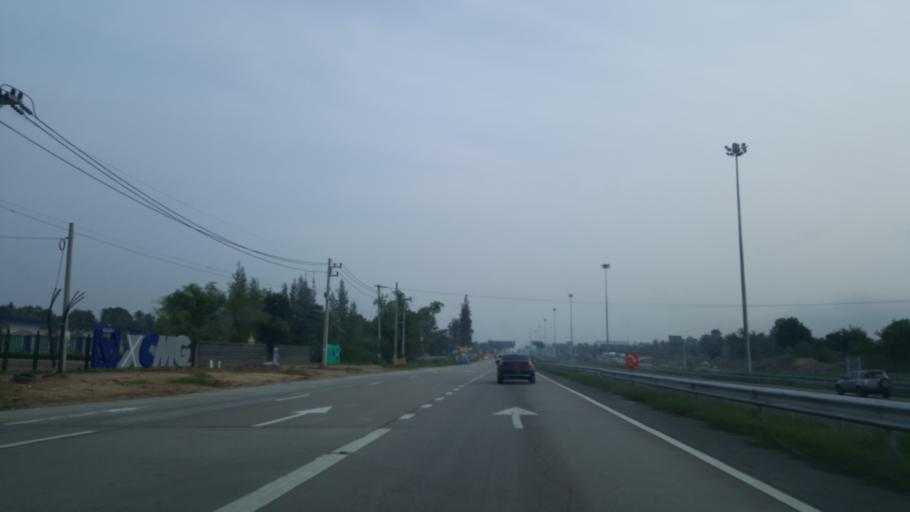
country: TH
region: Chon Buri
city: Bang Lamung
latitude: 12.9697
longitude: 100.9814
